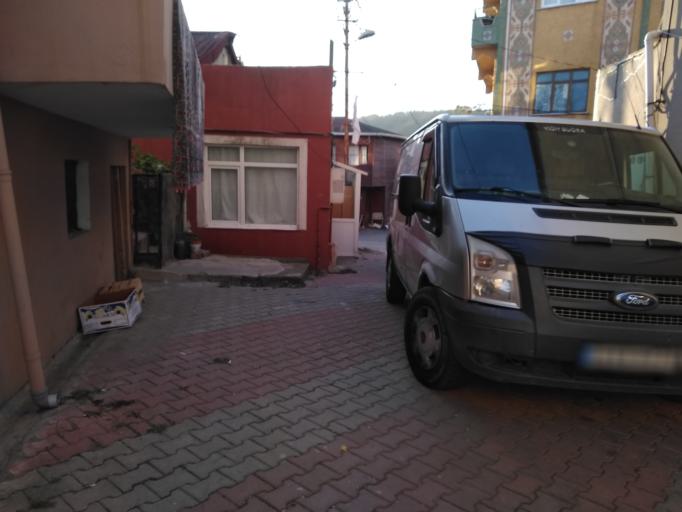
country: TR
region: Istanbul
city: Arikoey
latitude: 41.2365
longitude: 28.9836
